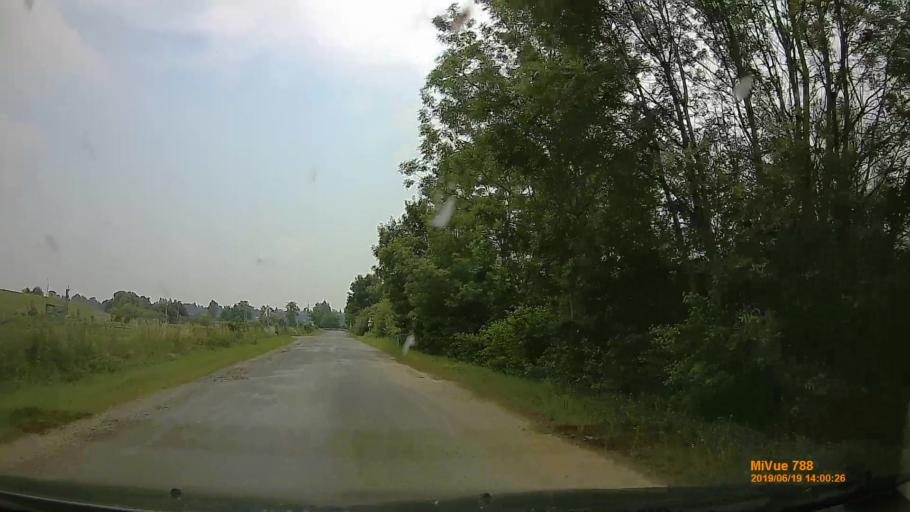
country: HU
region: Baranya
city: Szigetvar
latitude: 46.0836
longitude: 17.8038
